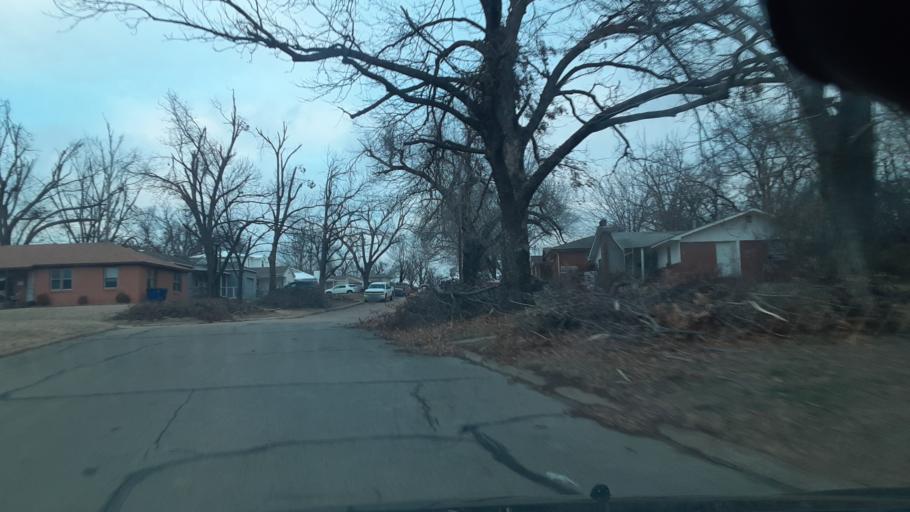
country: US
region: Oklahoma
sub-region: Logan County
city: Guthrie
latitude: 35.8900
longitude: -97.4197
